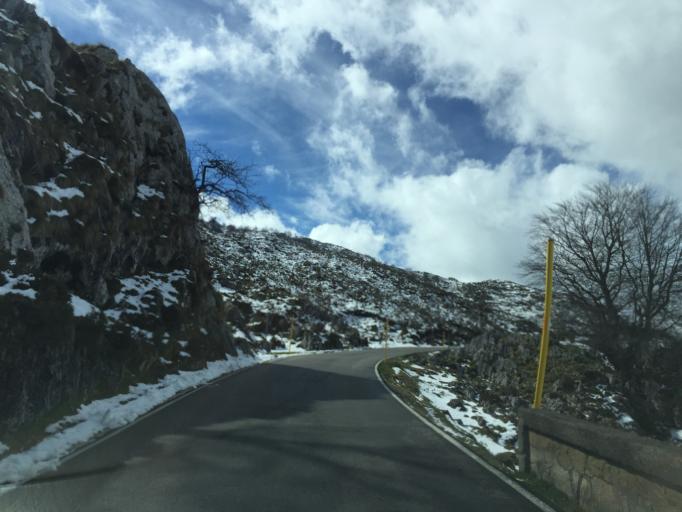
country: ES
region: Asturias
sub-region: Province of Asturias
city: Amieva
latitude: 43.2794
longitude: -5.0031
